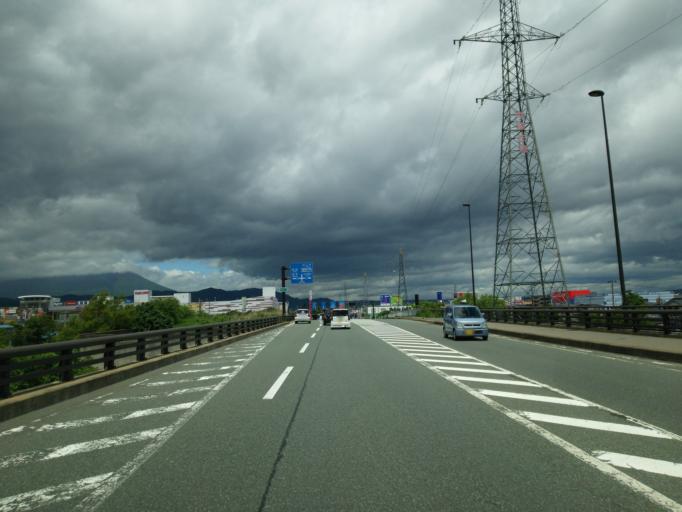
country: JP
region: Iwate
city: Morioka-shi
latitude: 39.7077
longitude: 141.1016
